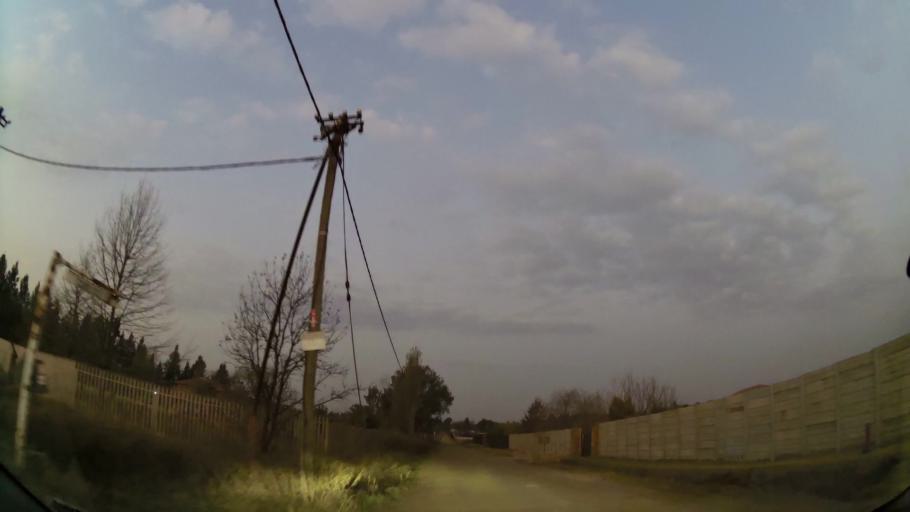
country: ZA
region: Gauteng
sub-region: Ekurhuleni Metropolitan Municipality
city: Benoni
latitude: -26.1132
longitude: 28.3070
